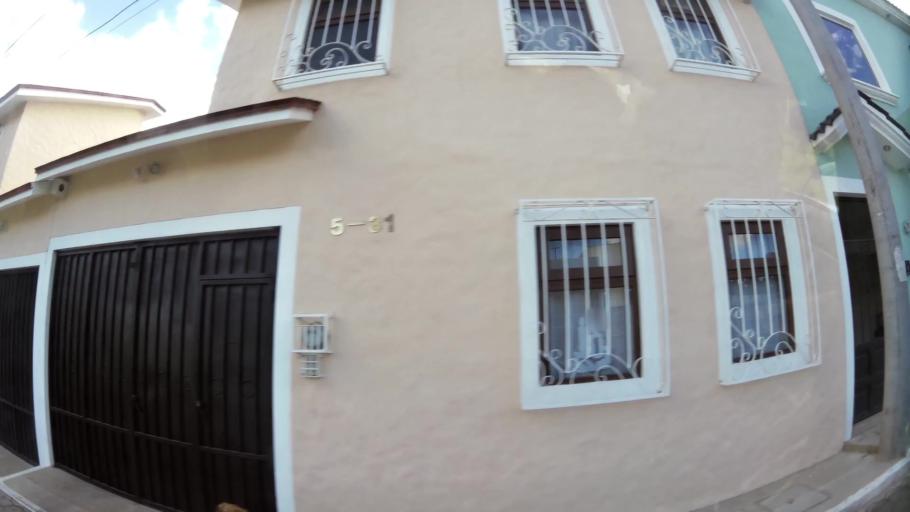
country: GT
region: Quetzaltenango
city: Quetzaltenango
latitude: 14.8348
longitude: -91.5512
